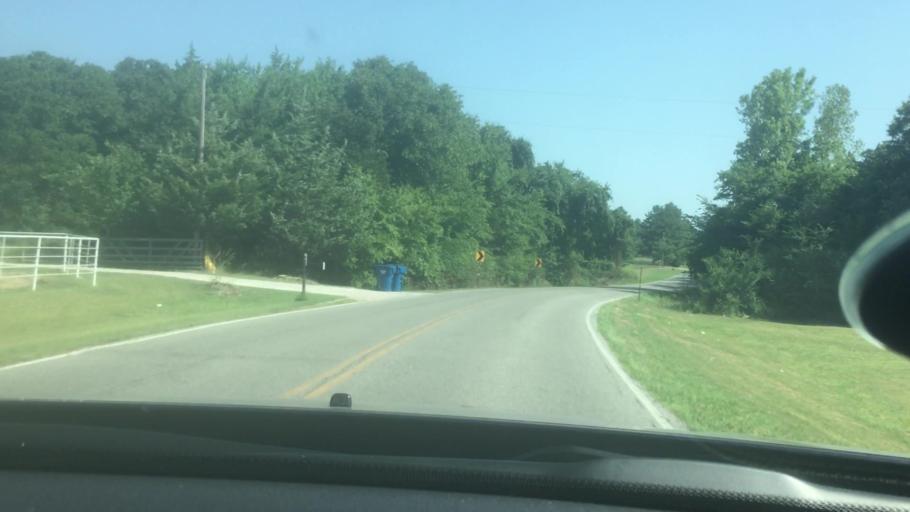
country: US
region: Oklahoma
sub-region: Bryan County
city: Calera
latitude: 34.0278
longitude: -96.4744
